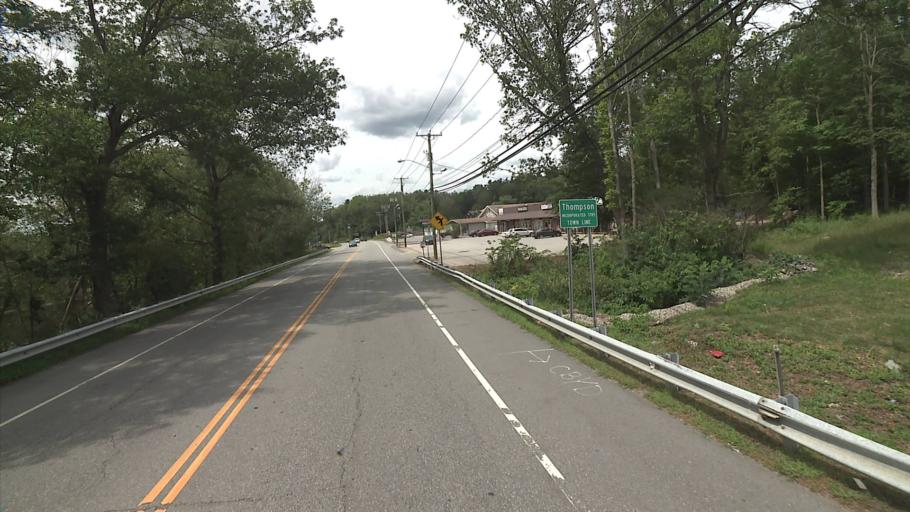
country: US
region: Connecticut
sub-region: Windham County
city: Putnam
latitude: 41.9321
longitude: -71.9317
